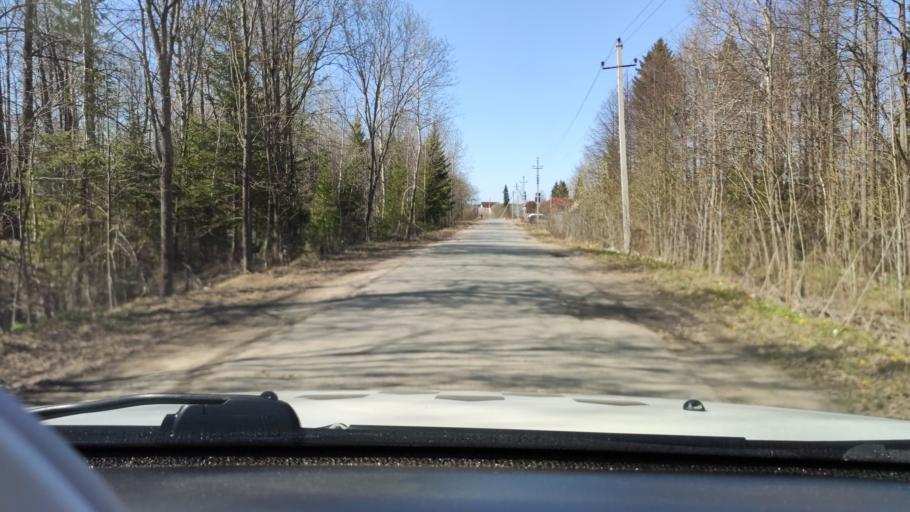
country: RU
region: Perm
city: Novyye Lyady
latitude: 58.0423
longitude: 56.6206
